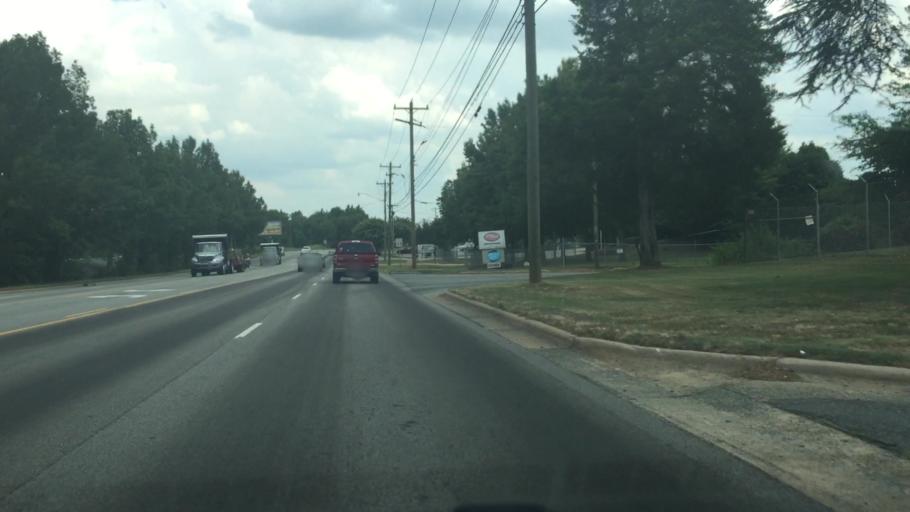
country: US
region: North Carolina
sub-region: Rowan County
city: Franklin
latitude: 35.6876
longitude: -80.5097
